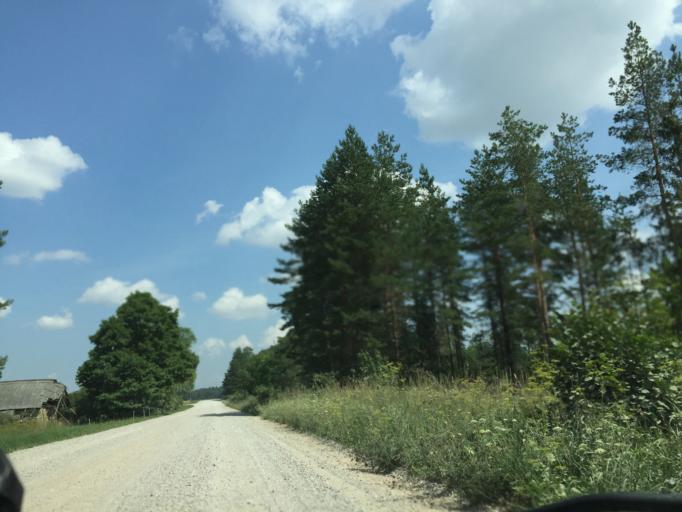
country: LT
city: Zagare
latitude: 56.3746
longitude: 23.2782
